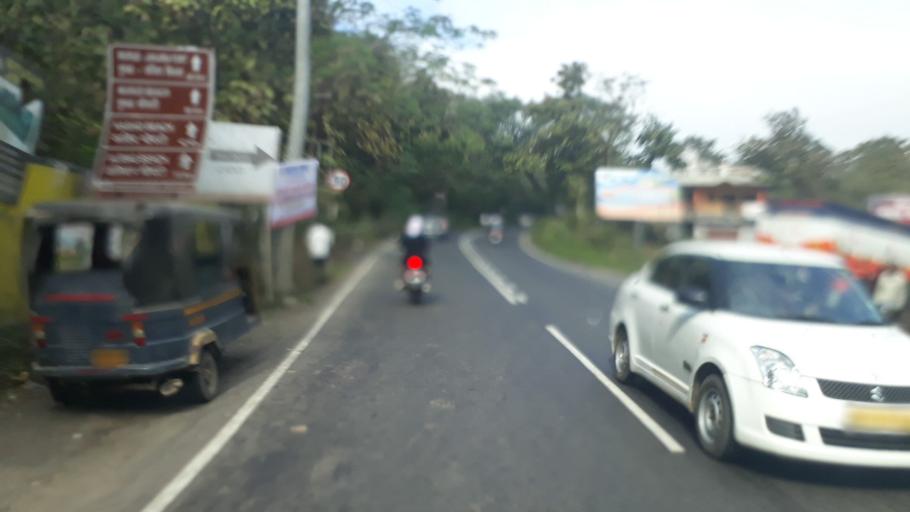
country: IN
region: Maharashtra
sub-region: Raigarh
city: Alibag
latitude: 18.6955
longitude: 72.9308
